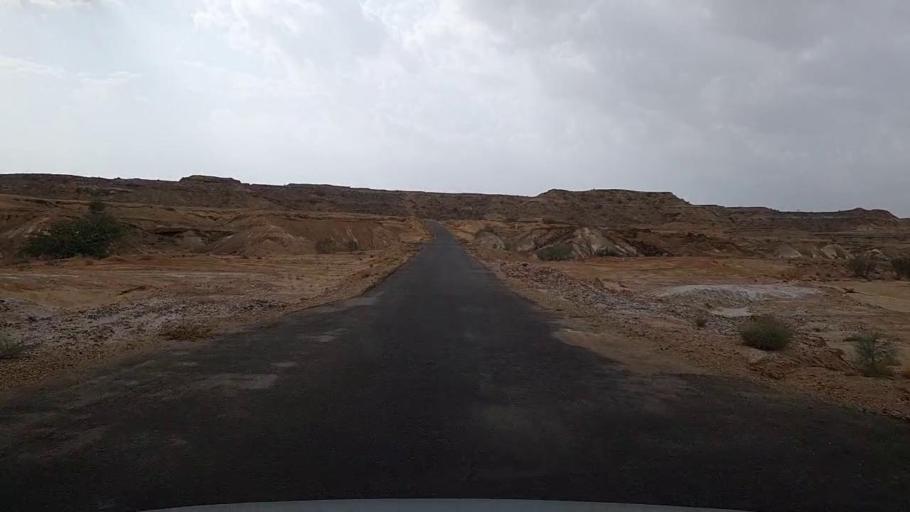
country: PK
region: Sindh
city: Jamshoro
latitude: 25.4206
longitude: 67.6929
